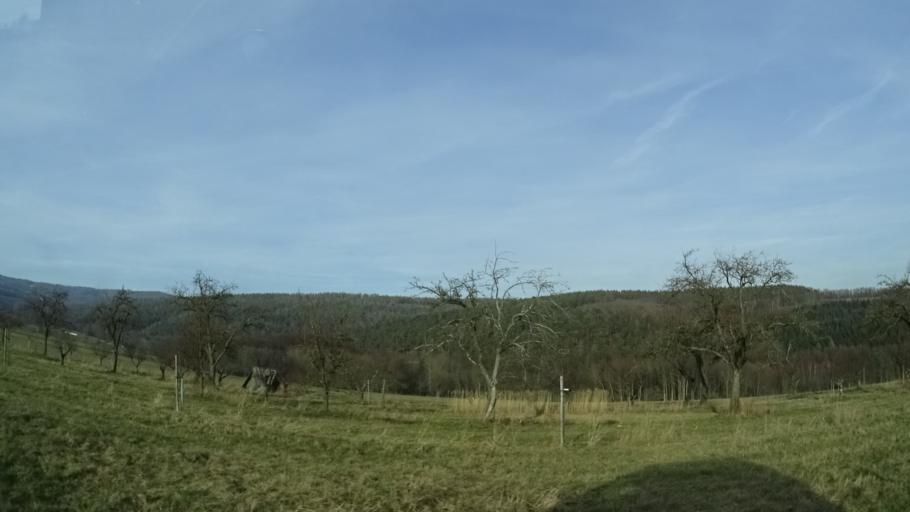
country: DE
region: Bavaria
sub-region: Regierungsbezirk Unterfranken
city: Sandberg
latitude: 50.3424
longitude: 10.0170
